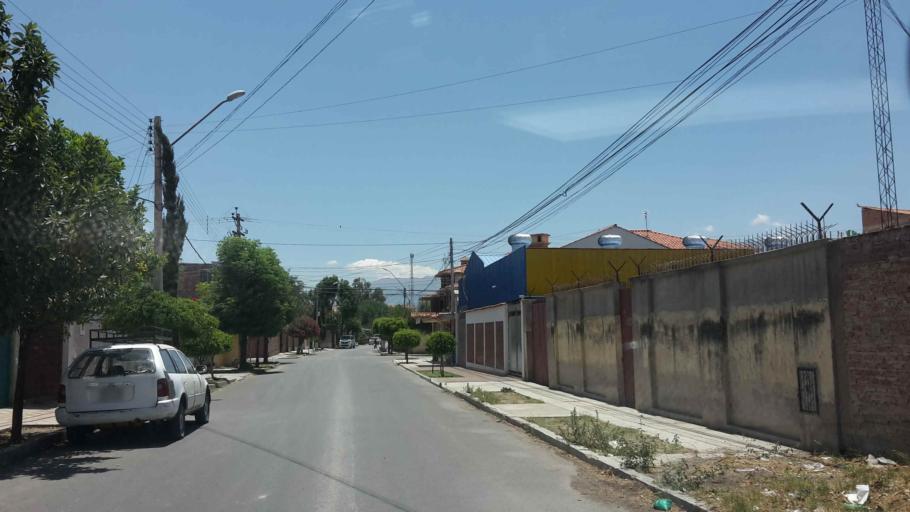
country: BO
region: Cochabamba
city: Cochabamba
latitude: -17.3772
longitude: -66.1935
